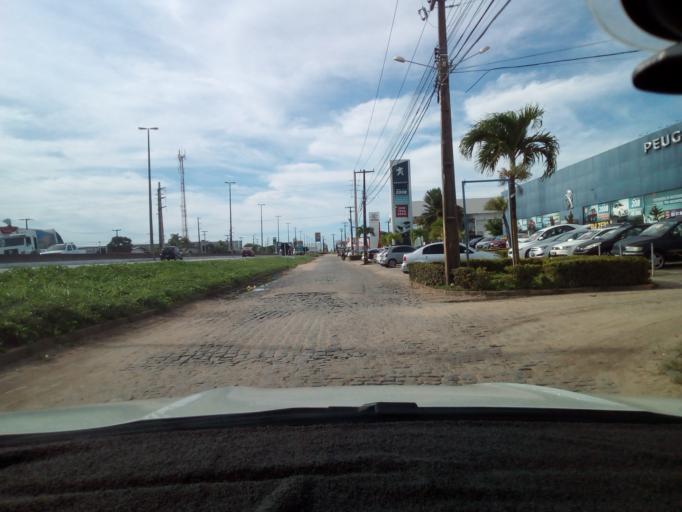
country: BR
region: Paraiba
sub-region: Joao Pessoa
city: Joao Pessoa
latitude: -7.0804
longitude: -34.8489
